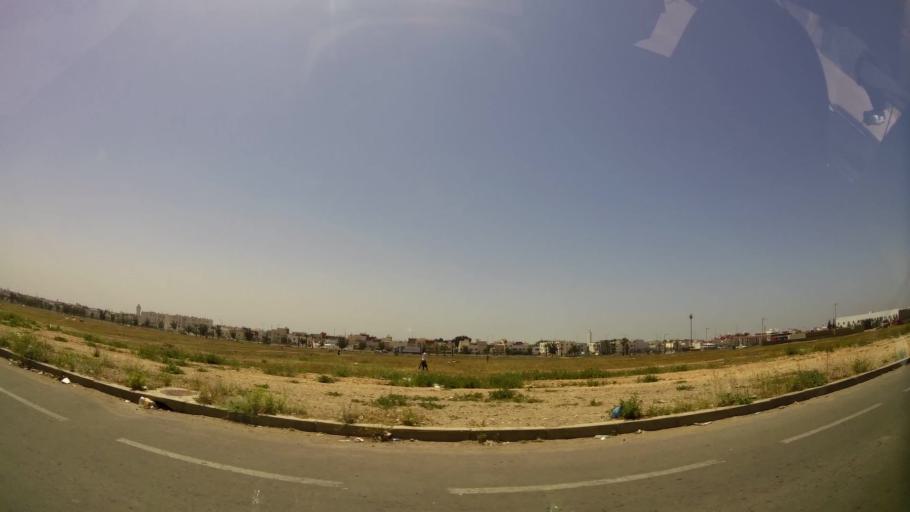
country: MA
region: Oued ed Dahab-Lagouira
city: Dakhla
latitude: 30.4287
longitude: -9.5616
